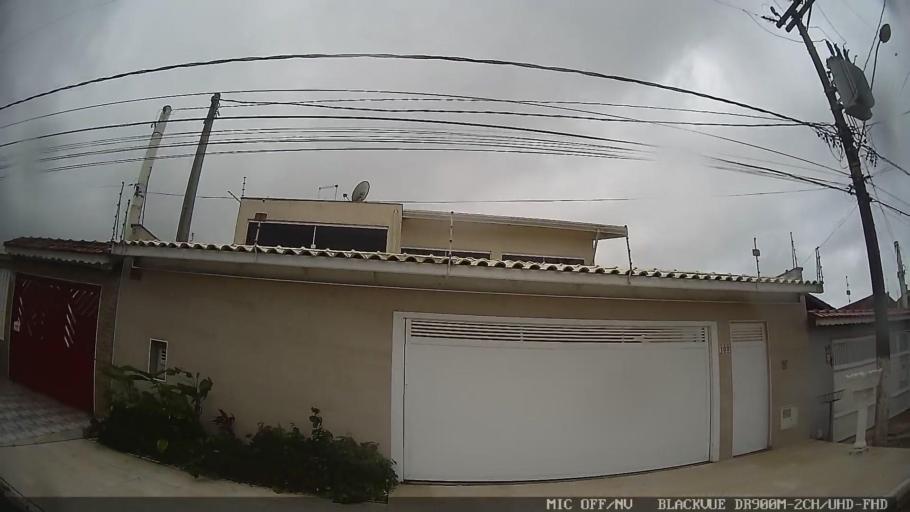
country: BR
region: Sao Paulo
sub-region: Mongagua
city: Mongagua
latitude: -24.1382
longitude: -46.7037
